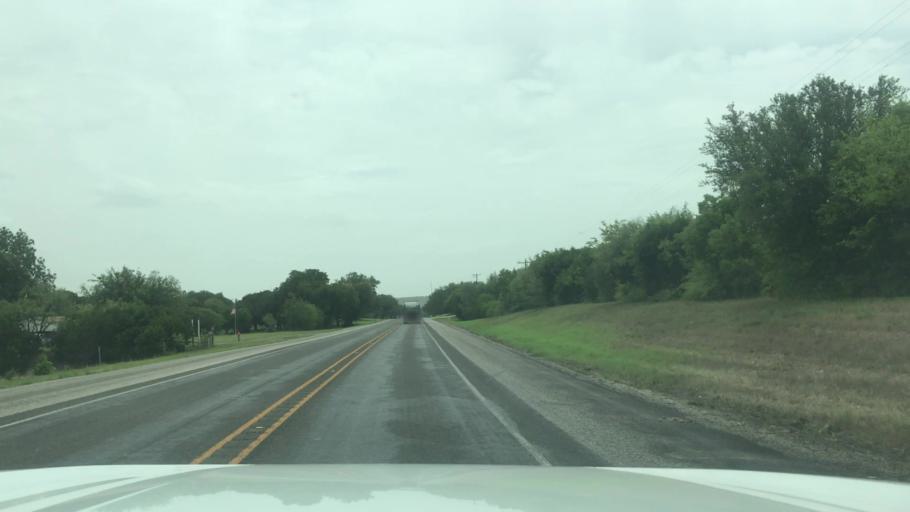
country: US
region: Texas
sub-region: Bosque County
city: Meridian
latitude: 31.8952
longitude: -97.6475
